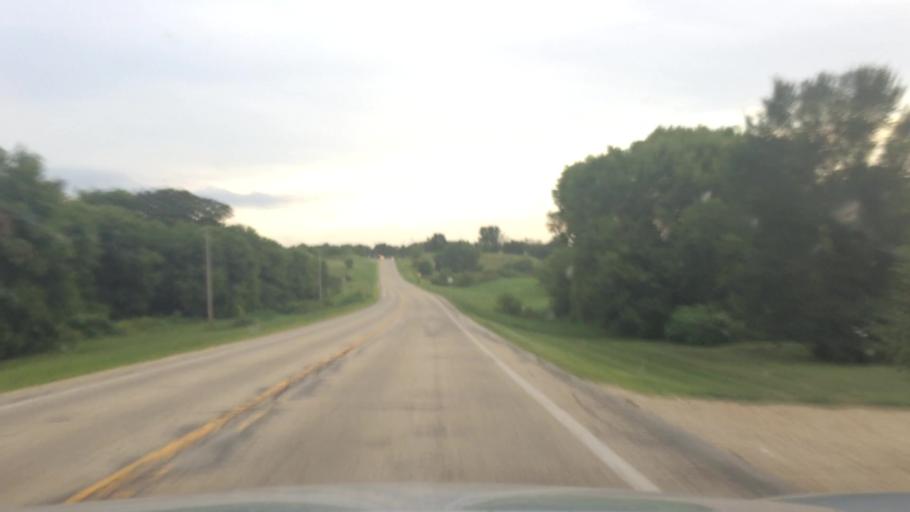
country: US
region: Wisconsin
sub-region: Dane County
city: Waunakee
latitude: 43.2070
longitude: -89.5488
